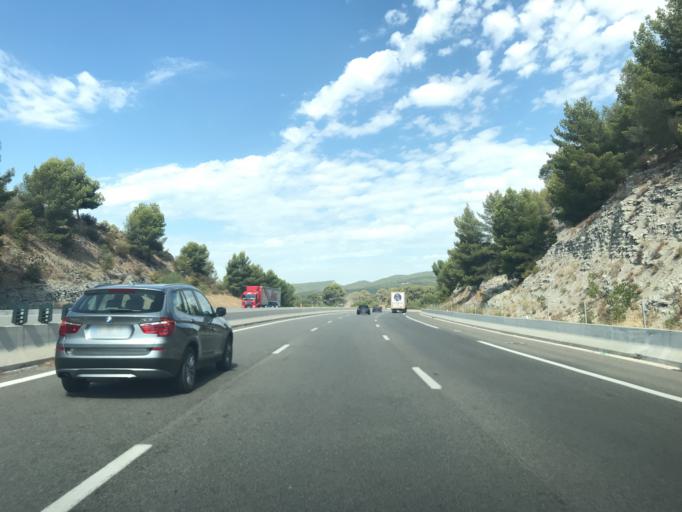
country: FR
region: Provence-Alpes-Cote d'Azur
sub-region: Departement des Bouches-du-Rhone
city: Ceyreste
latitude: 43.1990
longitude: 5.6369
